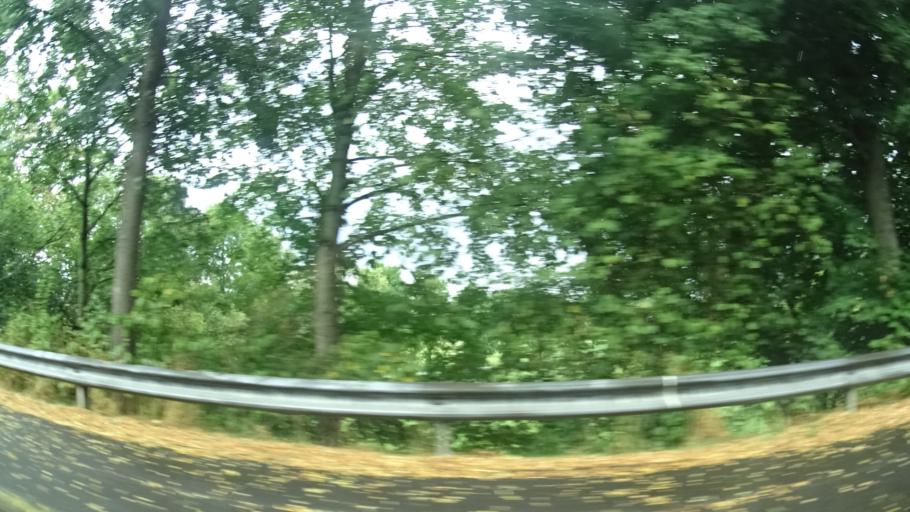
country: DE
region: Hesse
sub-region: Regierungsbezirk Kassel
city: Bad Hersfeld
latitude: 50.8318
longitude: 9.6742
